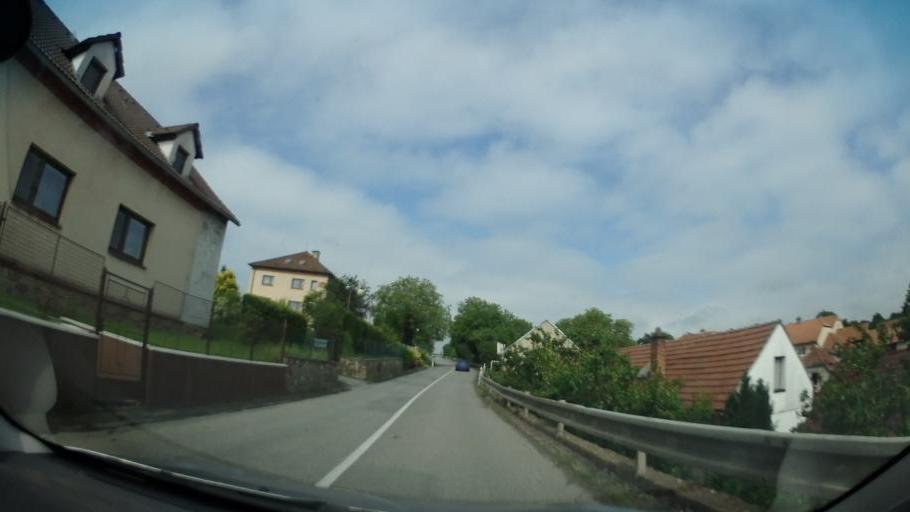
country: CZ
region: South Moravian
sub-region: Okres Brno-Venkov
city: Dolni Loucky
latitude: 49.3786
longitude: 16.3517
